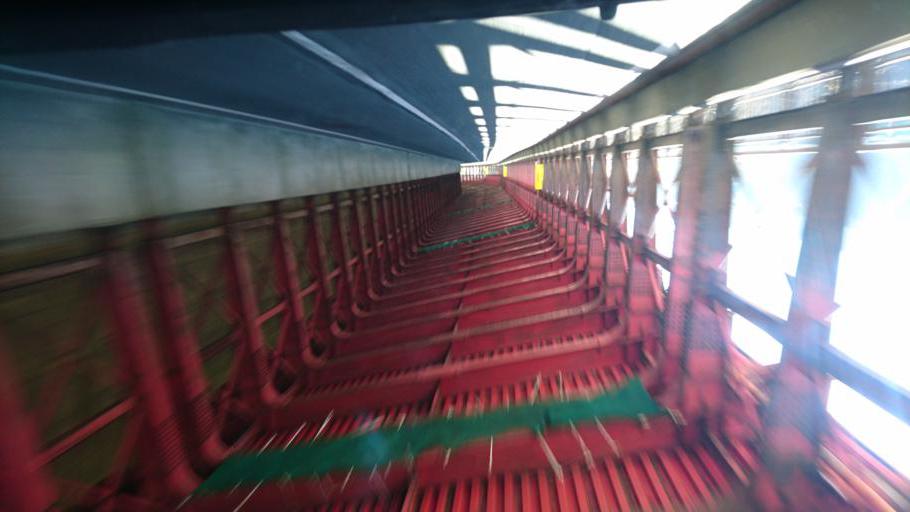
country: JP
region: Iwate
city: Kitakami
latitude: 39.3049
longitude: 140.8848
